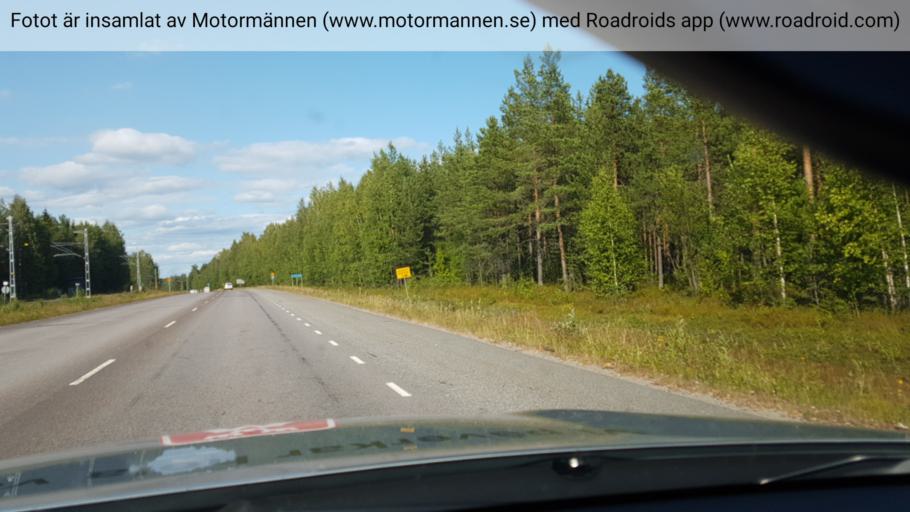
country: SE
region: Norrbotten
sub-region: Pitea Kommun
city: Pitea
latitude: 65.2934
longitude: 21.5083
